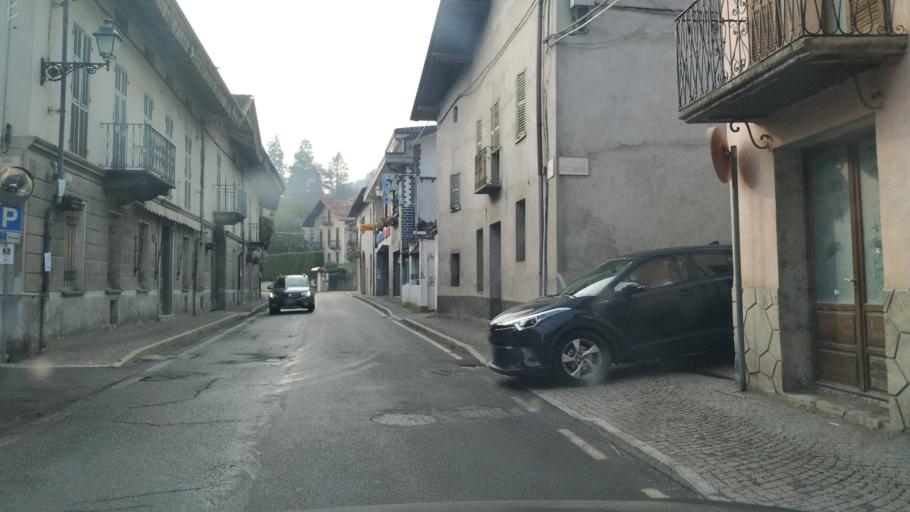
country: IT
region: Piedmont
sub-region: Provincia di Cuneo
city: Roccavione
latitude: 44.3146
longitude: 7.4836
